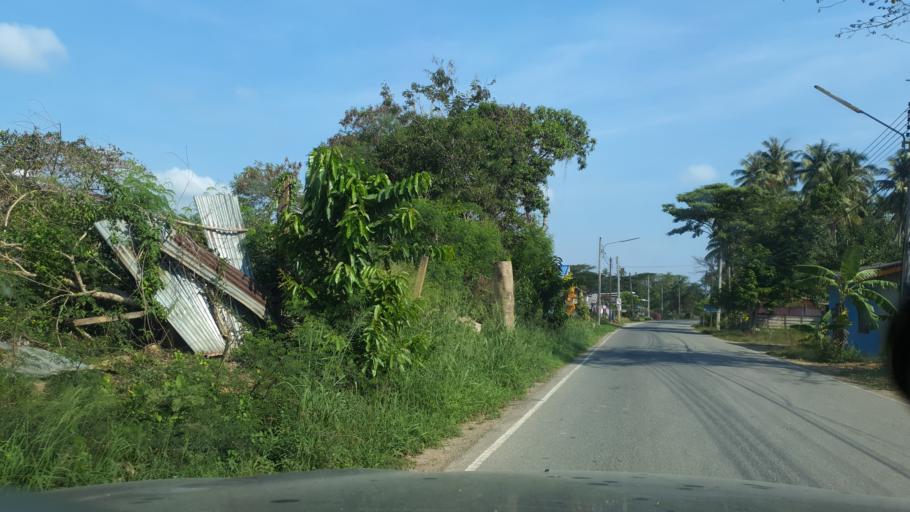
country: TH
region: Prachuap Khiri Khan
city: Bang Saphan
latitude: 11.3452
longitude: 99.5567
